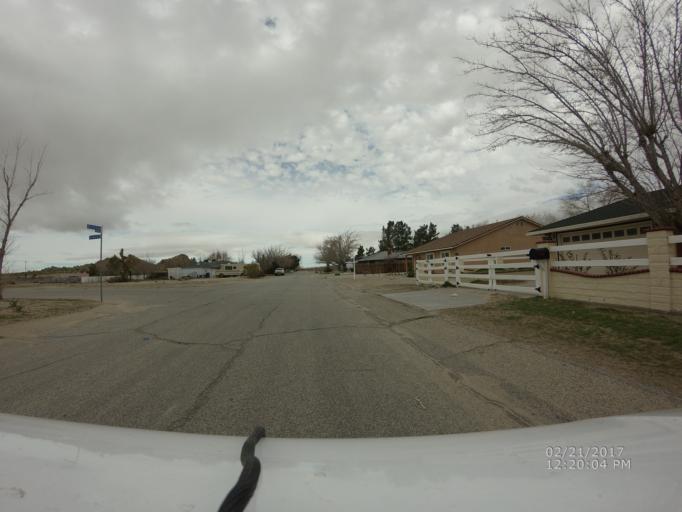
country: US
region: California
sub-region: Los Angeles County
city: Lake Los Angeles
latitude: 34.6346
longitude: -117.8612
